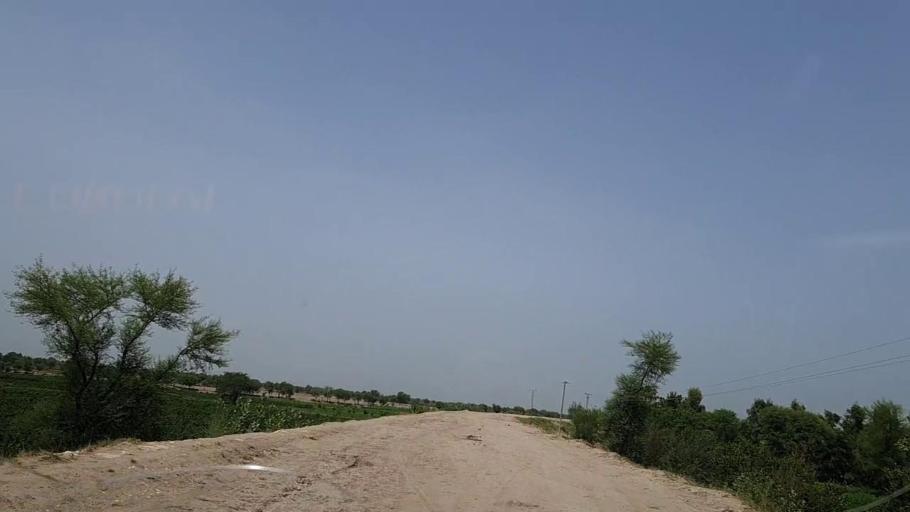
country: PK
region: Sindh
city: Tharu Shah
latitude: 27.0140
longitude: 68.1026
